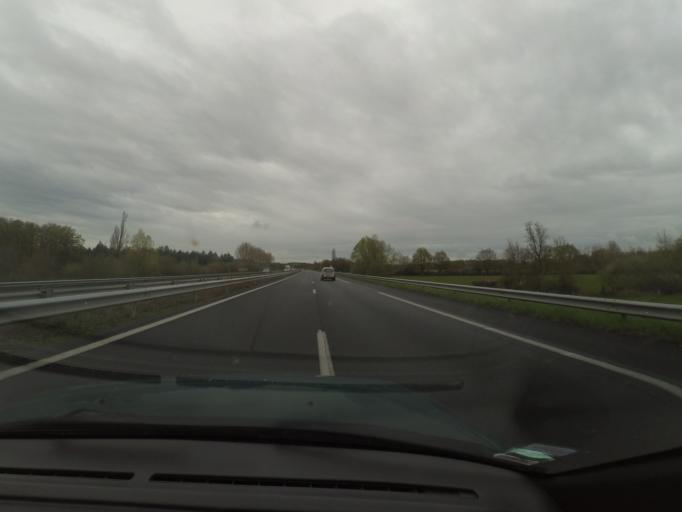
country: FR
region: Pays de la Loire
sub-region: Departement de Maine-et-Loire
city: Durtal
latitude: 47.6938
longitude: -0.2494
